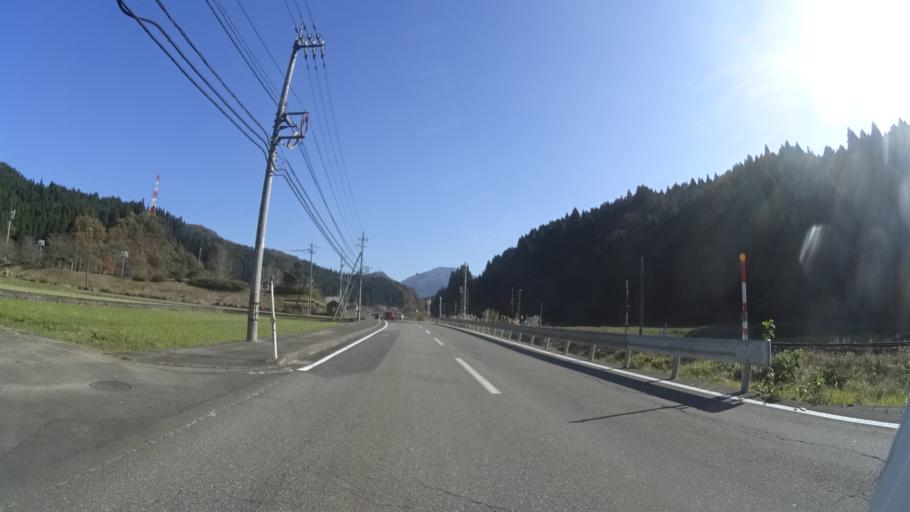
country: JP
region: Fukui
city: Ono
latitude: 36.0063
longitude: 136.3985
